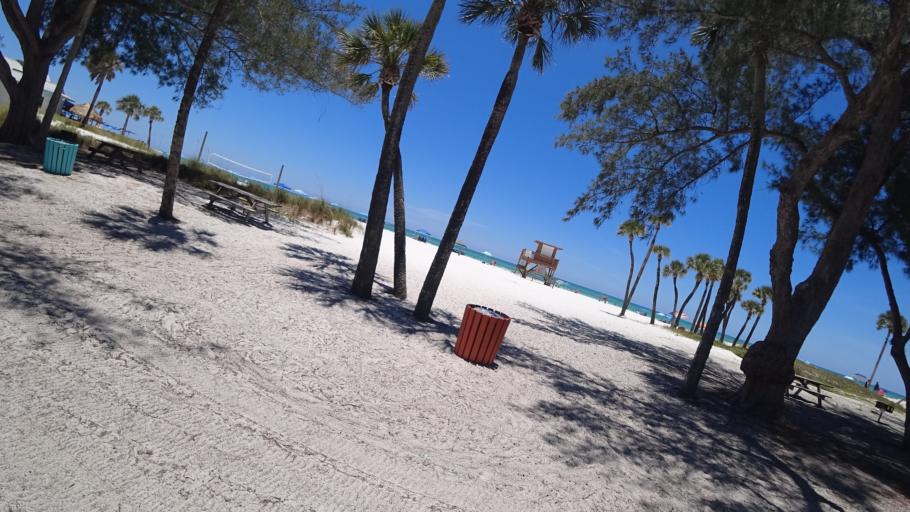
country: US
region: Florida
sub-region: Manatee County
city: Cortez
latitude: 27.4515
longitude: -82.6928
